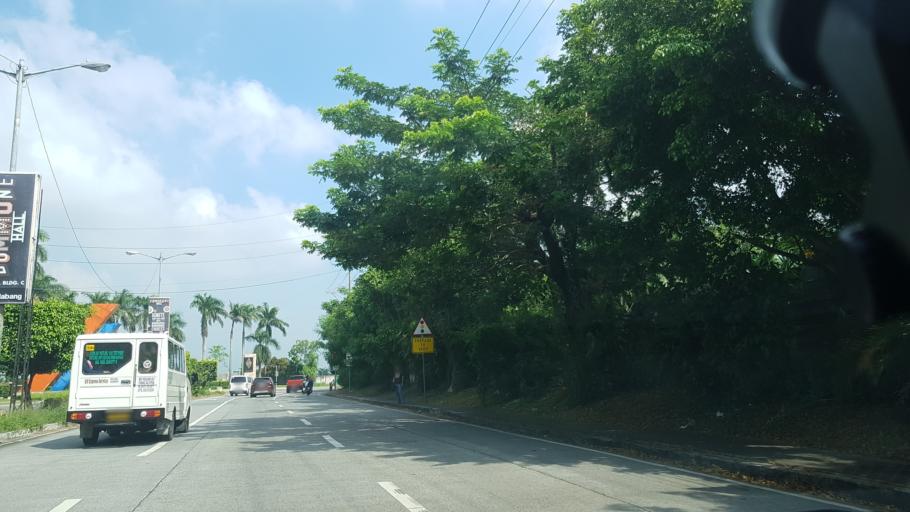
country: PH
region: Calabarzon
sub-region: Province of Laguna
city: San Pedro
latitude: 14.3841
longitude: 121.0109
